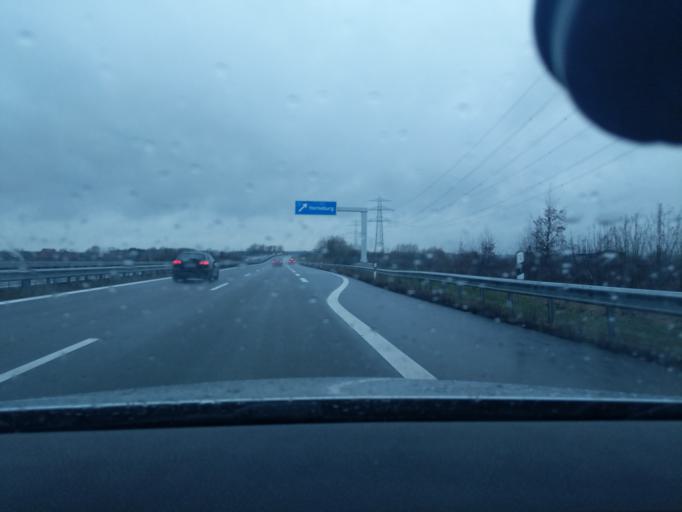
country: DE
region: Lower Saxony
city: Neuenkirchen
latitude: 53.5130
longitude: 9.6021
